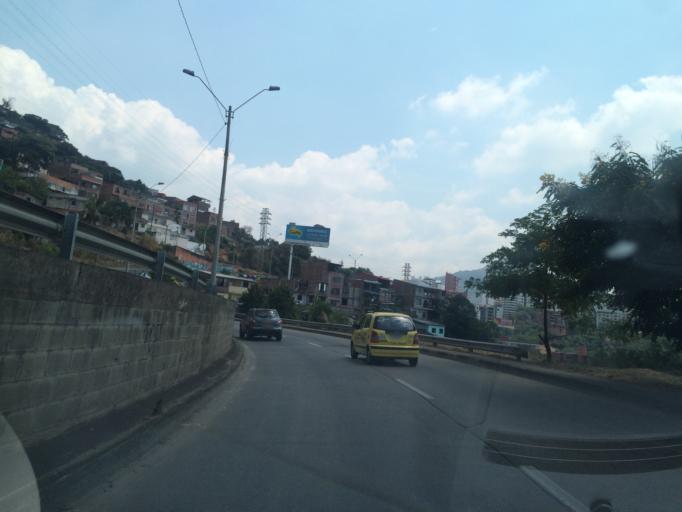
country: CO
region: Valle del Cauca
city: Cali
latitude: 3.4397
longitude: -76.5488
